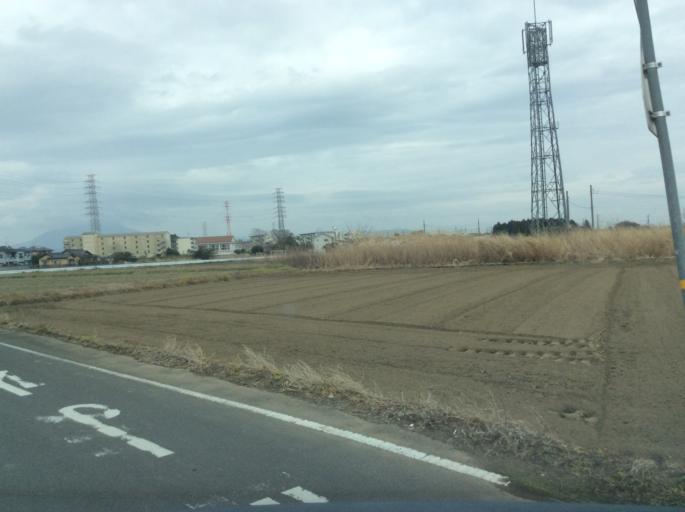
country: JP
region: Ibaraki
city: Ishige
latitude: 36.1721
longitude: 139.9551
